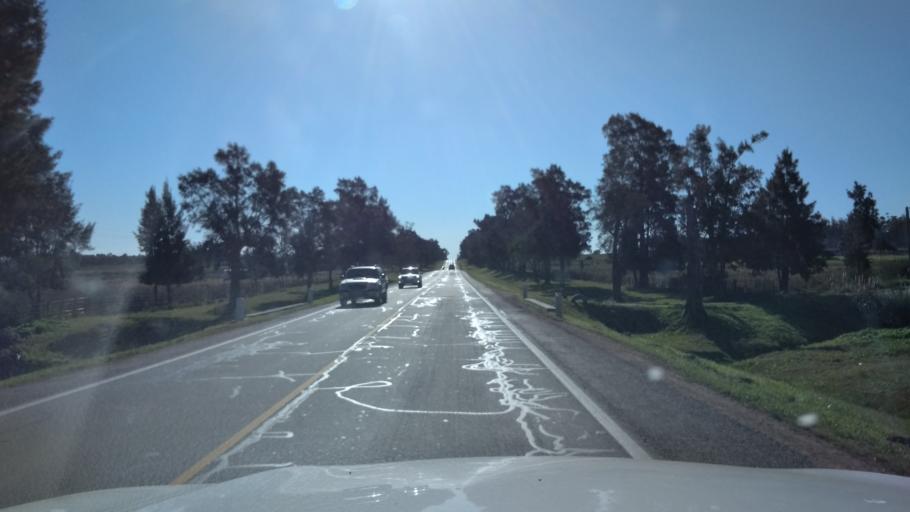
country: UY
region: Canelones
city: San Jacinto
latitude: -34.5945
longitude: -55.8328
